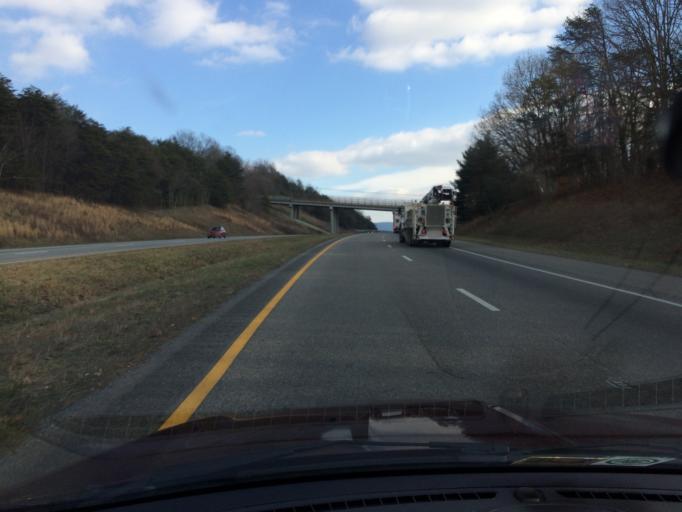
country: US
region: Virginia
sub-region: Alleghany County
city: Clifton Forge
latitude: 37.8304
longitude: -79.8232
